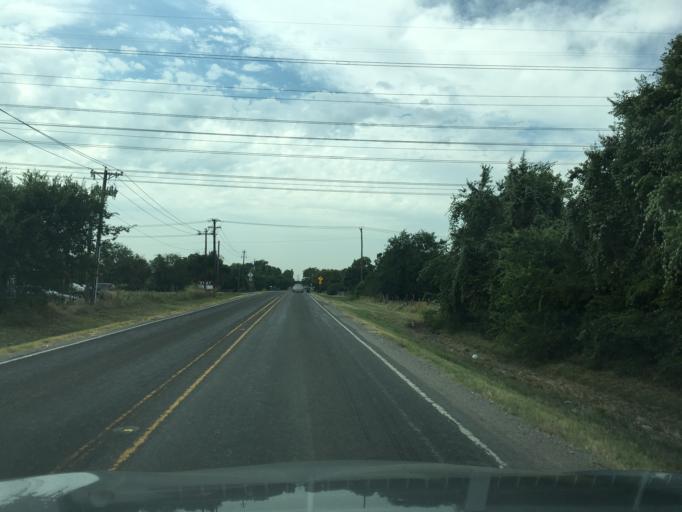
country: US
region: Texas
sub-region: Collin County
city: Parker
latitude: 33.0617
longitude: -96.6191
